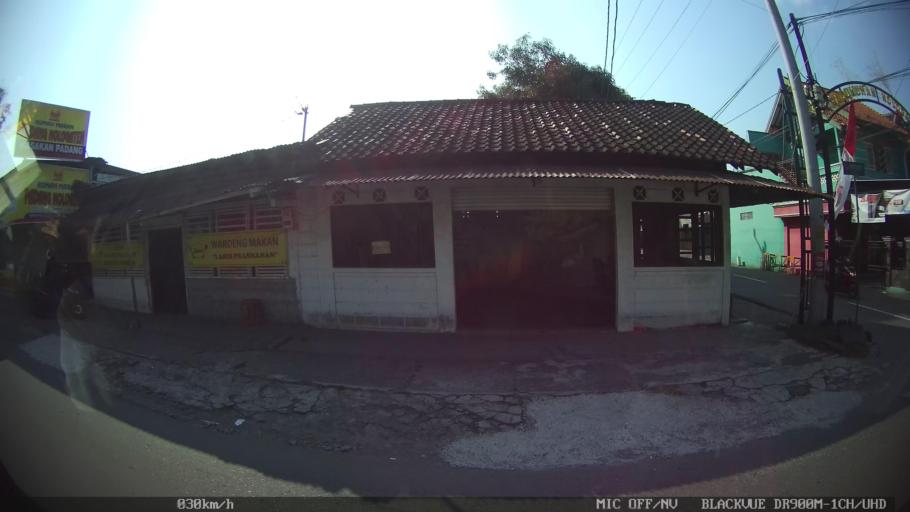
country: ID
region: Daerah Istimewa Yogyakarta
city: Depok
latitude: -7.7763
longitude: 110.4005
